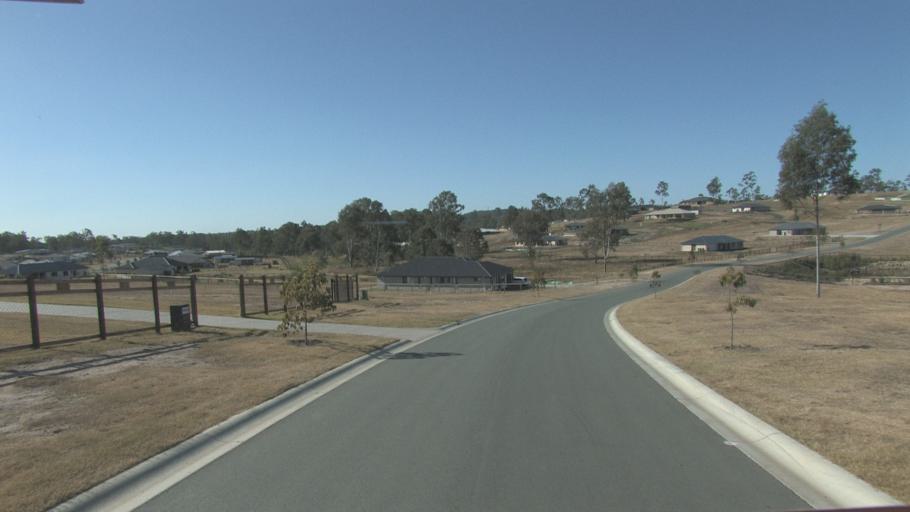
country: AU
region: Queensland
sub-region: Logan
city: Cedar Vale
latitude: -27.8739
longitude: 153.0473
